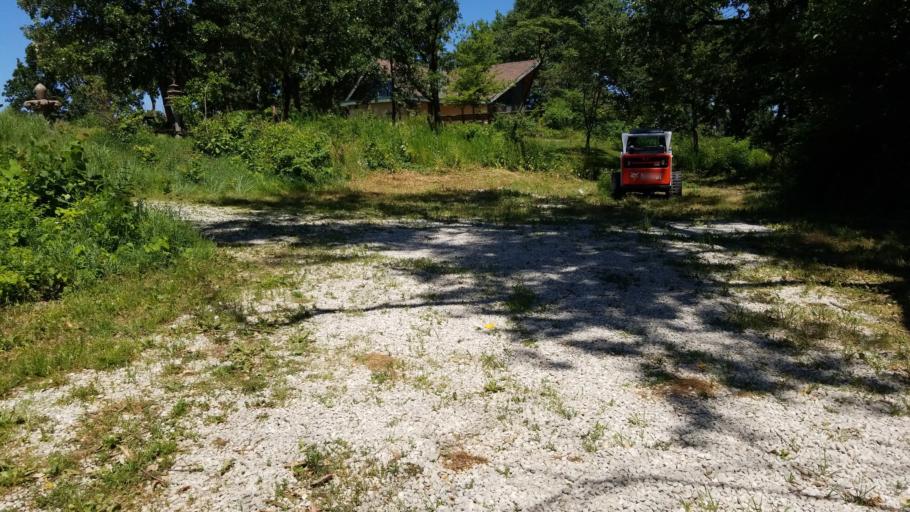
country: US
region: Iowa
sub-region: Pottawattamie County
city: Carter Lake
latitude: 41.3892
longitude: -95.9511
